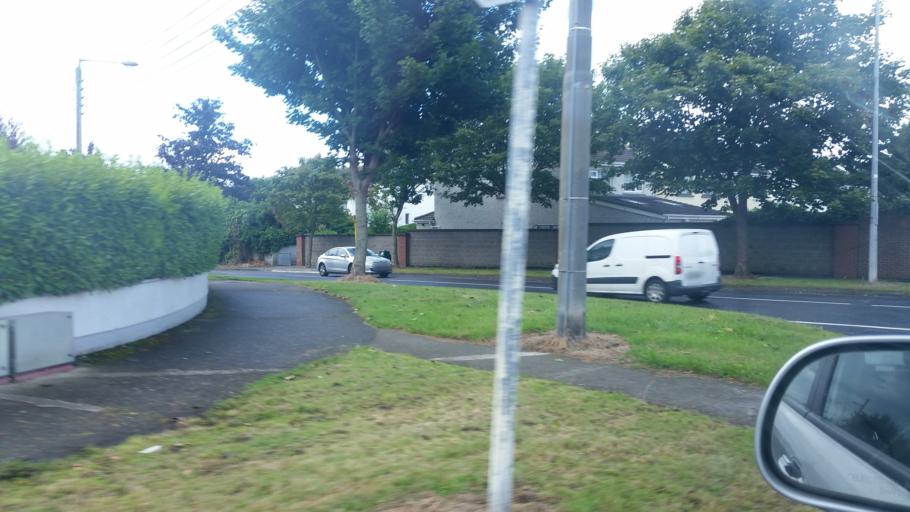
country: IE
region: Leinster
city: Portmarnock
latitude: 53.4291
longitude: -6.1332
